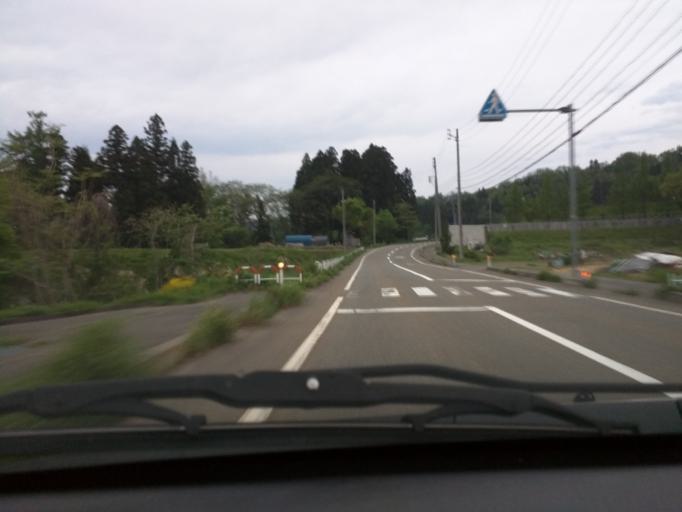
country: JP
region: Niigata
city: Ojiya
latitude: 37.3098
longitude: 138.7716
